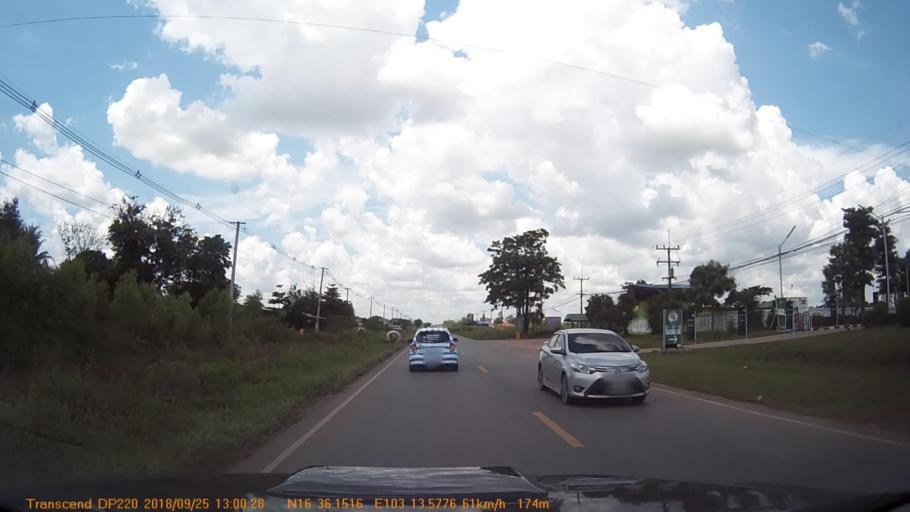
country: TH
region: Kalasin
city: Huai Mek
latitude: 16.6027
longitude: 103.2262
